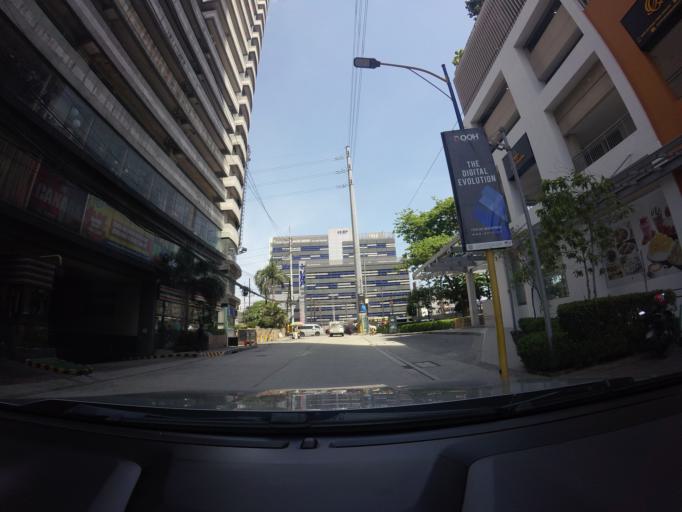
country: PH
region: Metro Manila
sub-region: Mandaluyong
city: Mandaluyong City
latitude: 14.5764
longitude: 121.0509
